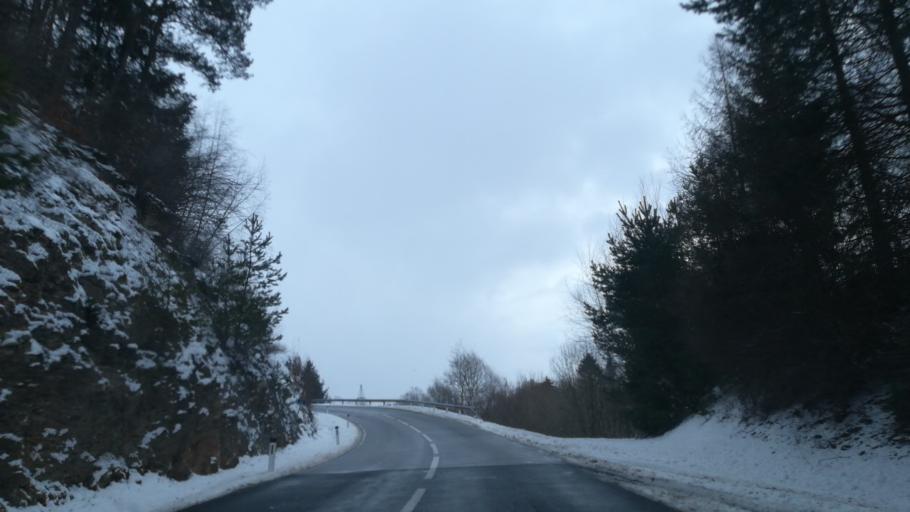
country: AT
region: Styria
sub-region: Politischer Bezirk Murtal
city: Poels
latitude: 47.2103
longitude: 14.5582
